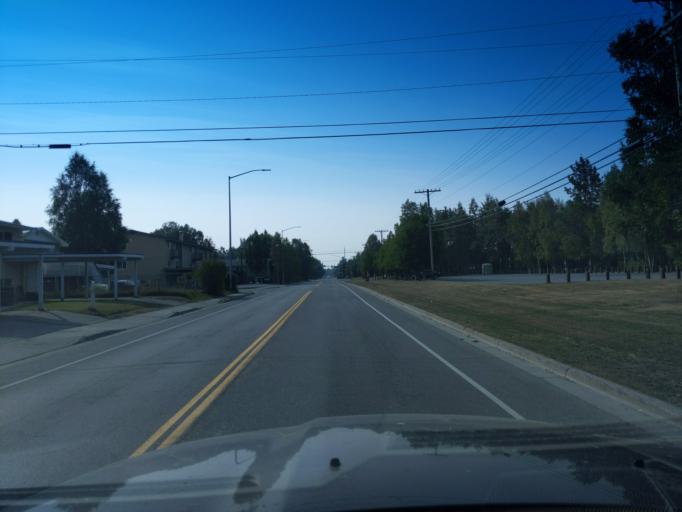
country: US
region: Alaska
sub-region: Anchorage Municipality
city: Anchorage
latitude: 61.1914
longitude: -149.9429
